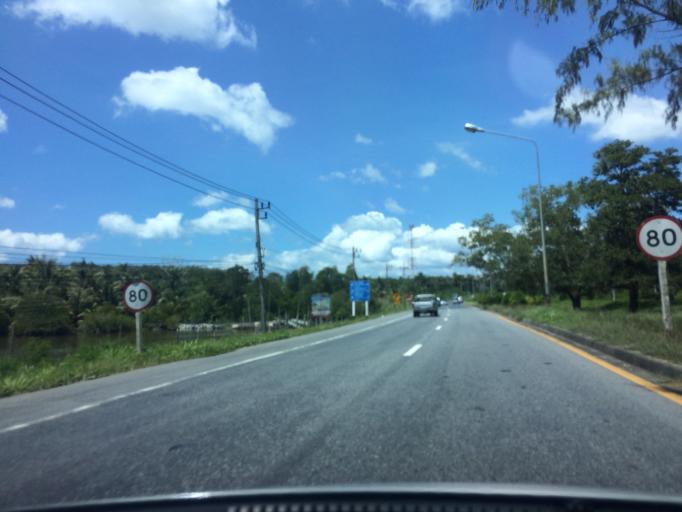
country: TH
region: Phuket
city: Thalang
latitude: 8.2109
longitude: 98.2982
